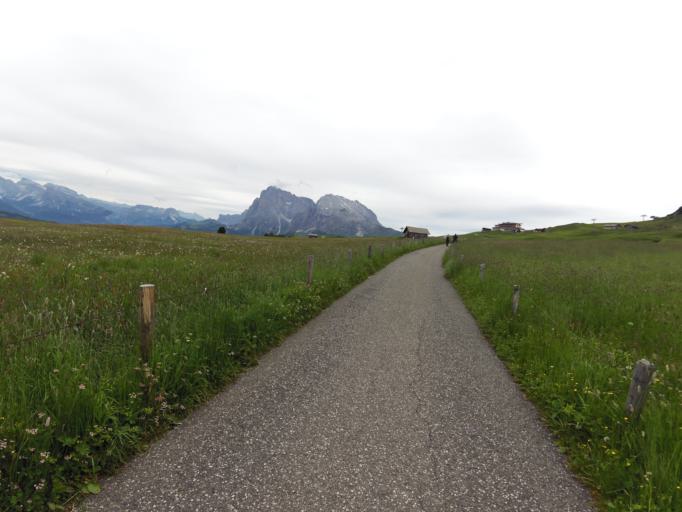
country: IT
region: Trentino-Alto Adige
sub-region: Bolzano
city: Ortisei
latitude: 46.5244
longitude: 11.6331
